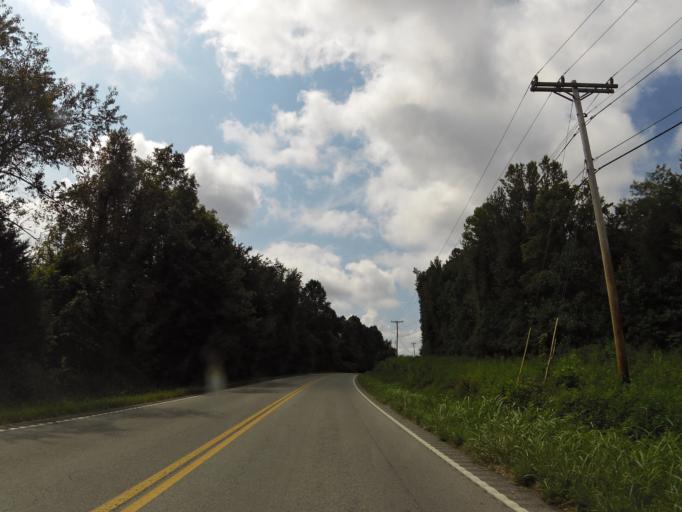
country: US
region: Tennessee
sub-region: Perry County
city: Linden
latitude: 35.6548
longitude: -87.8214
